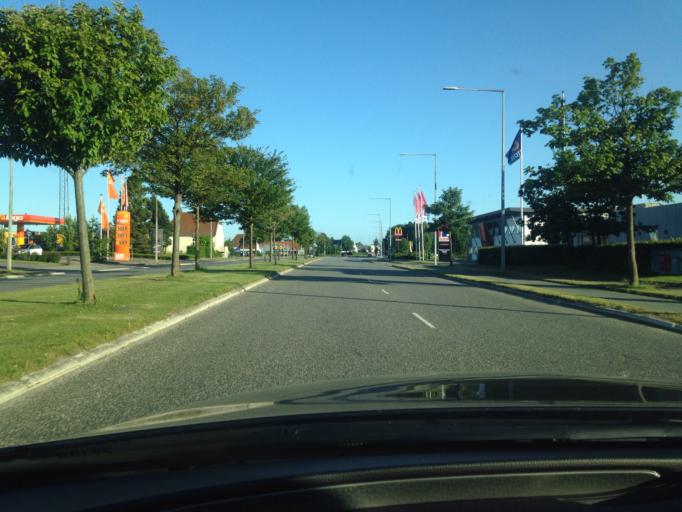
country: DK
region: South Denmark
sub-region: Kolding Kommune
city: Kolding
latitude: 55.5057
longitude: 9.4574
